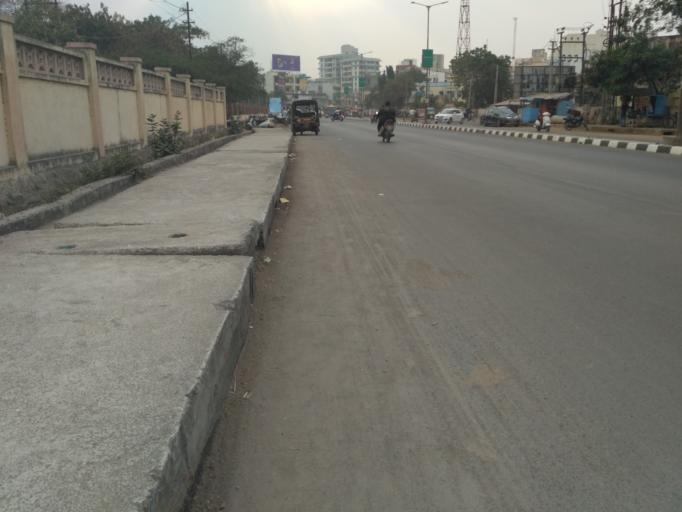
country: IN
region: Gujarat
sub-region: Porbandar
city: Porbandar
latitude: 21.6395
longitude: 69.6246
